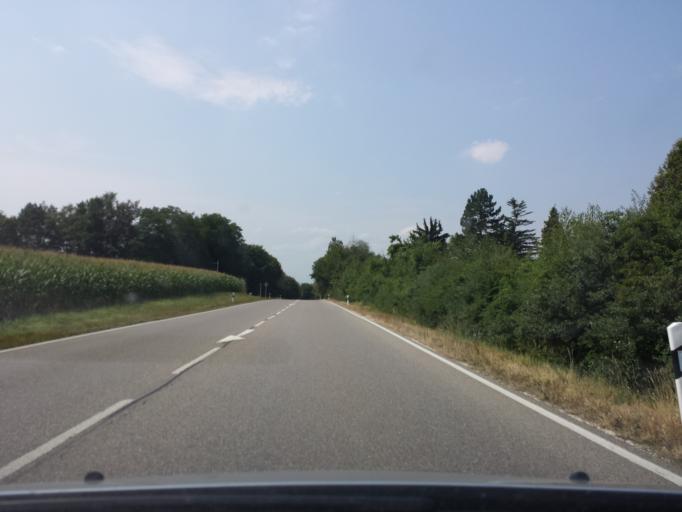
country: DE
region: Bavaria
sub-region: Swabia
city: Nersingen
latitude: 48.4295
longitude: 10.1510
